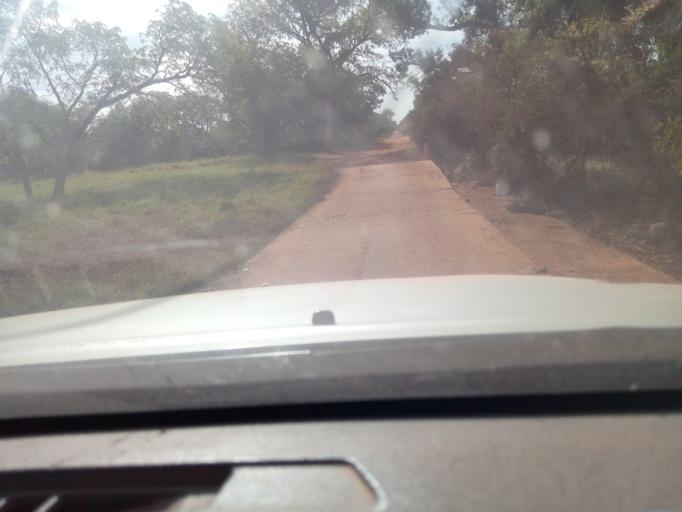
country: ML
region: Sikasso
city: Sikasso
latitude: 11.9318
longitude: -6.0733
